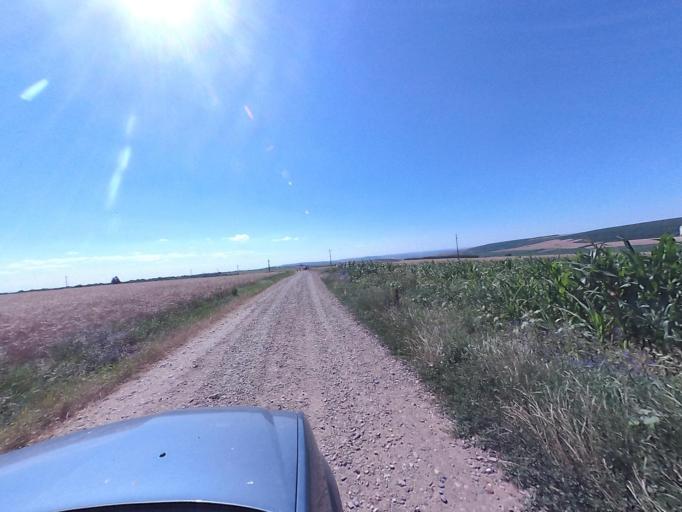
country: RO
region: Vaslui
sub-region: Comuna Costesti
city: Costesti
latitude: 46.4812
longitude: 27.7757
